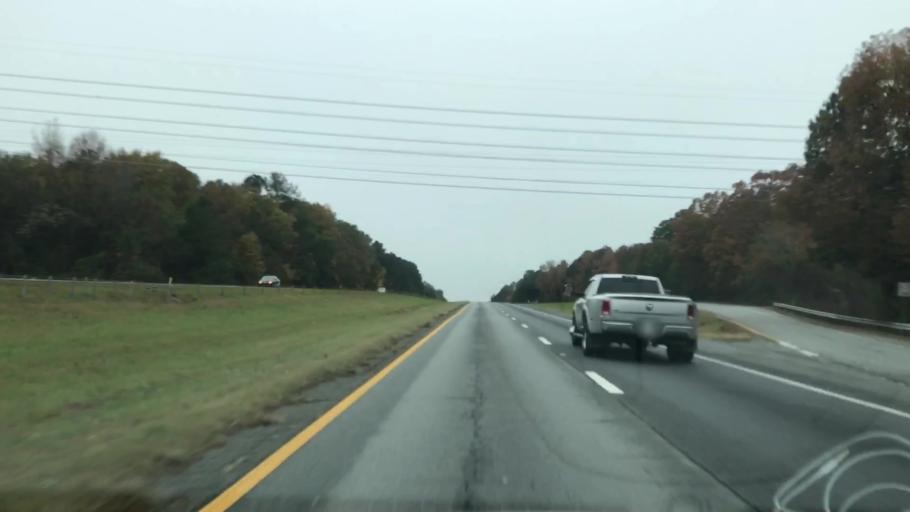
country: US
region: South Carolina
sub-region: Lexington County
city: Chapin
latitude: 34.2010
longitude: -81.3647
